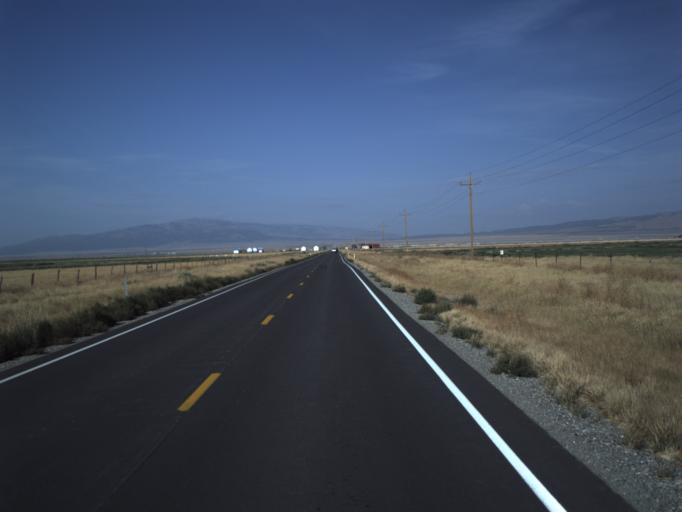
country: US
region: Idaho
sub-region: Oneida County
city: Malad City
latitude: 41.9671
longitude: -112.8555
